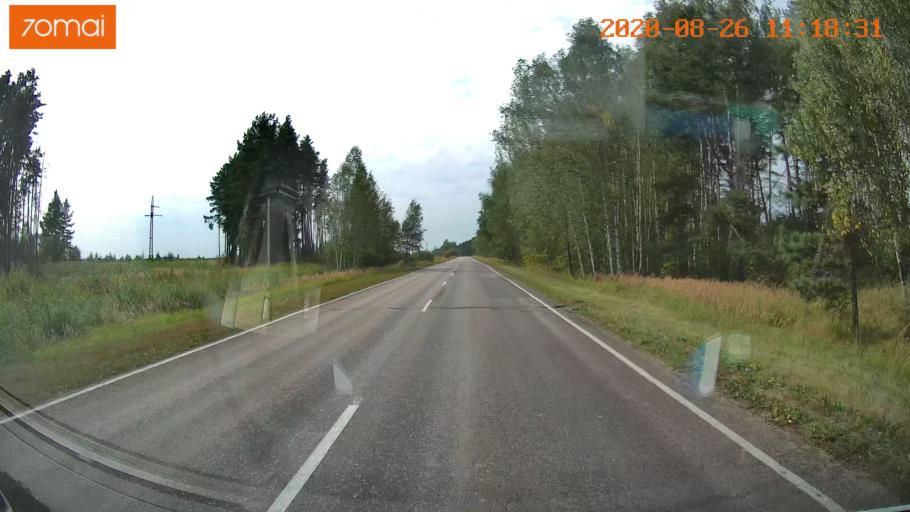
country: RU
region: Rjazan
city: Shilovo
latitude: 54.4092
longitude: 41.0959
